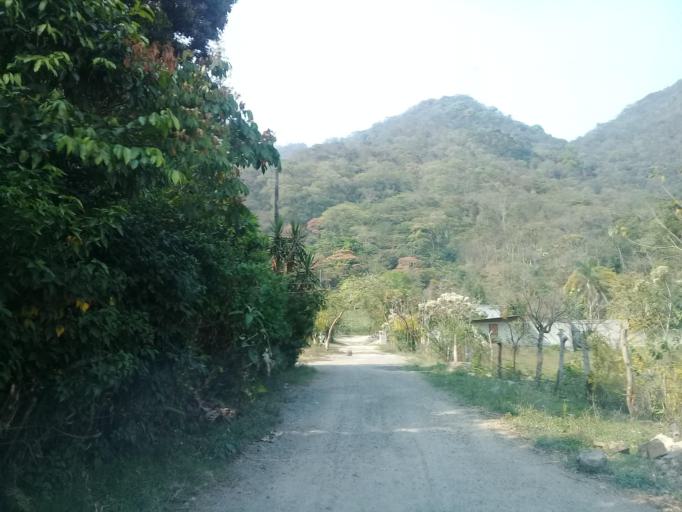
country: MX
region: Veracruz
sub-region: Ixtaczoquitlan
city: Campo Chico
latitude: 18.8374
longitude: -97.0262
